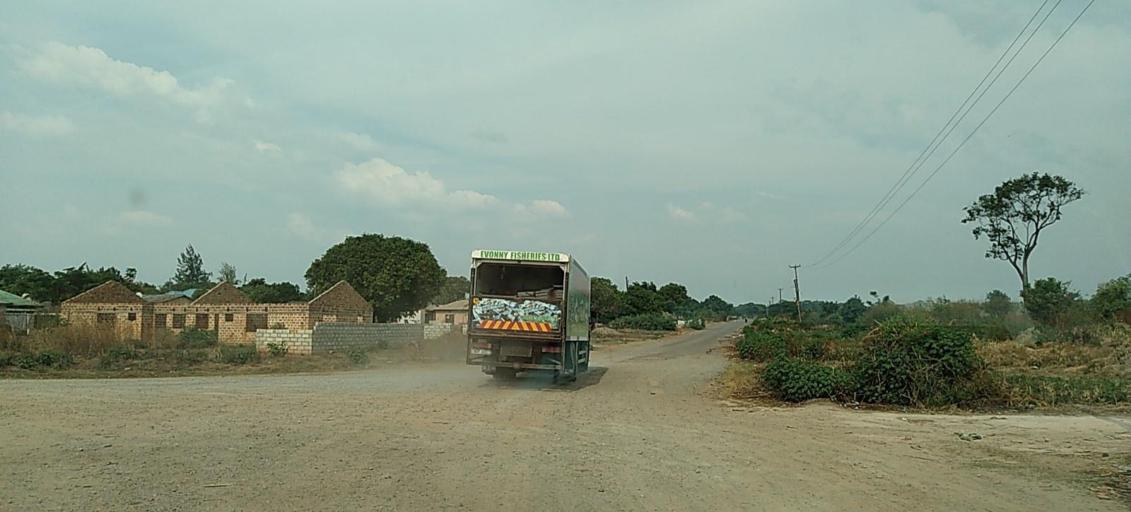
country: ZM
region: Copperbelt
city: Chililabombwe
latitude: -12.3732
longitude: 27.8163
